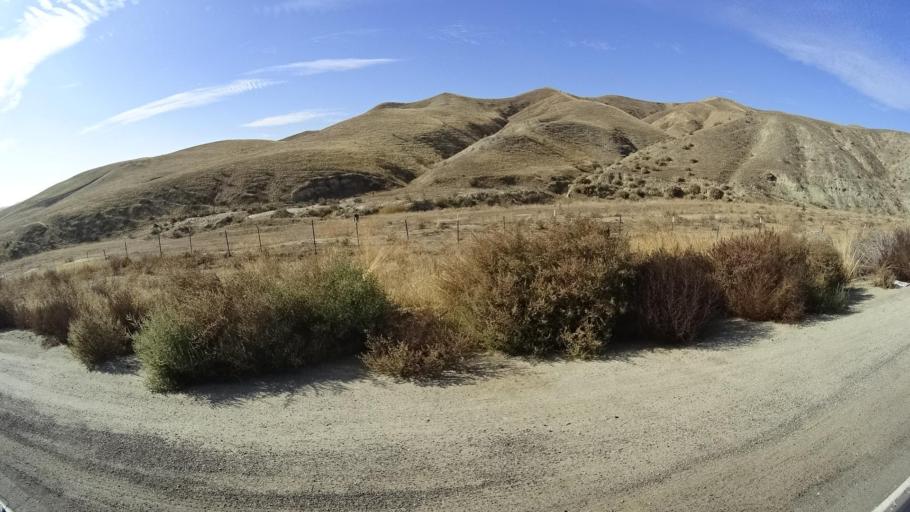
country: US
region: California
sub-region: Kern County
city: Oildale
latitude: 35.5366
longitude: -118.9599
